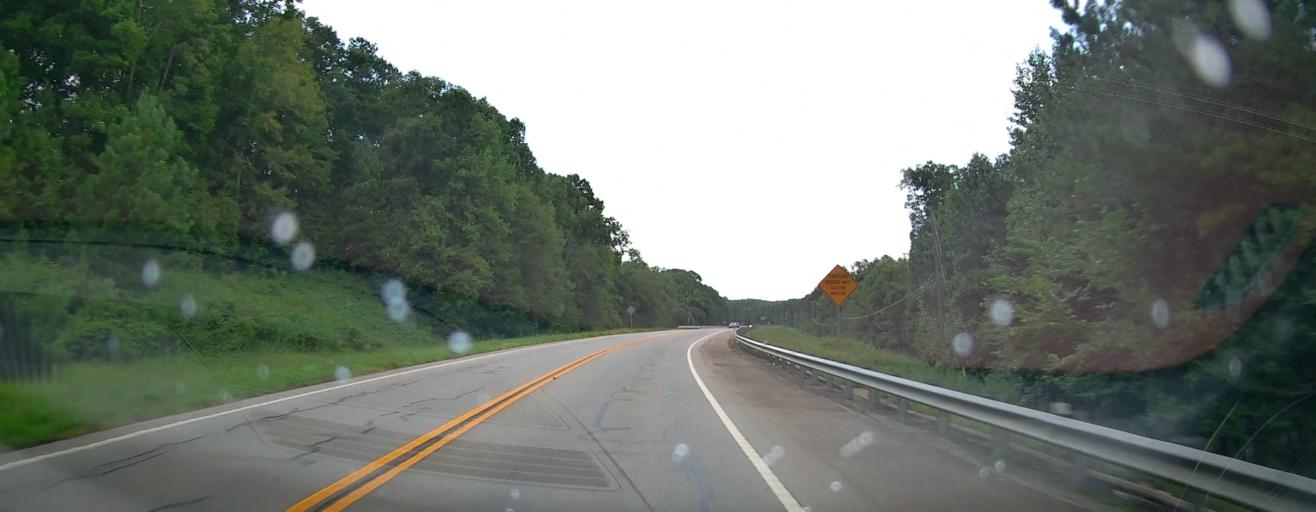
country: US
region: Georgia
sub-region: Coweta County
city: Senoia
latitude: 33.1771
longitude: -84.5815
